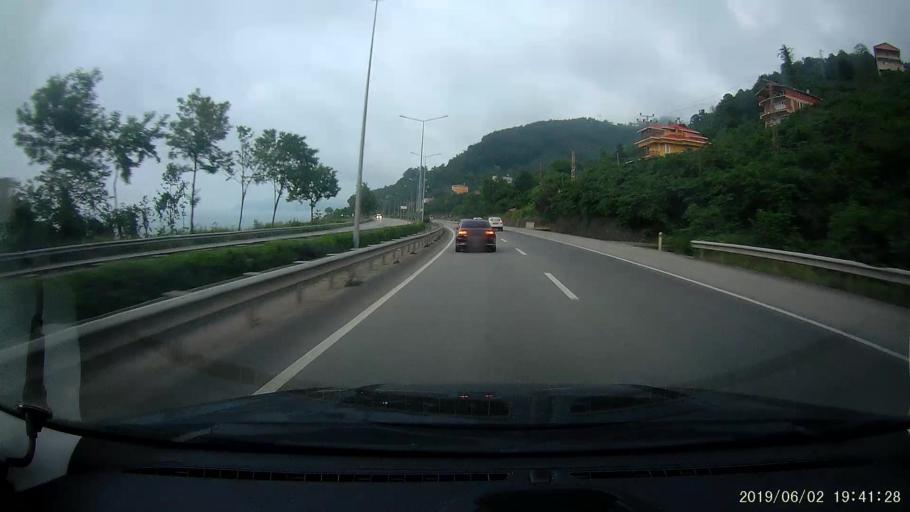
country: TR
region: Giresun
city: Kesap
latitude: 40.9135
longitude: 38.4810
